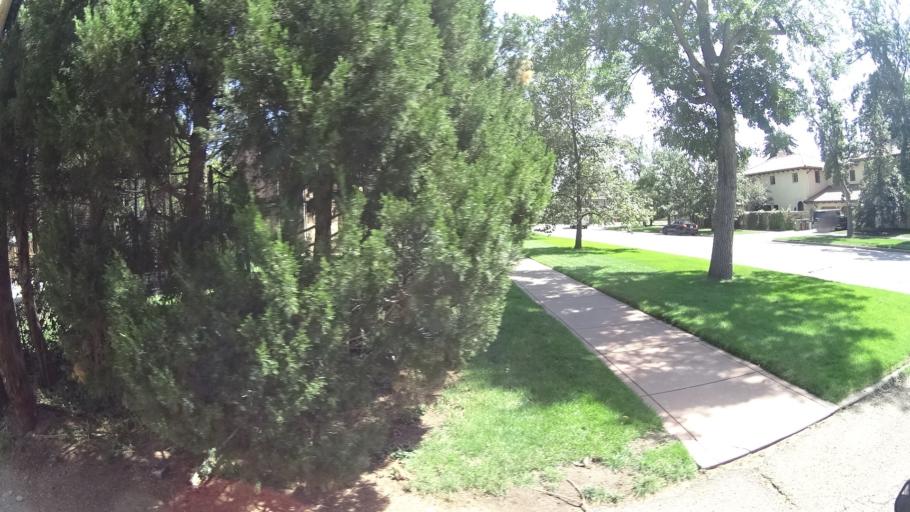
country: US
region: Colorado
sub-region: El Paso County
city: Colorado Springs
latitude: 38.8553
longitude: -104.8251
